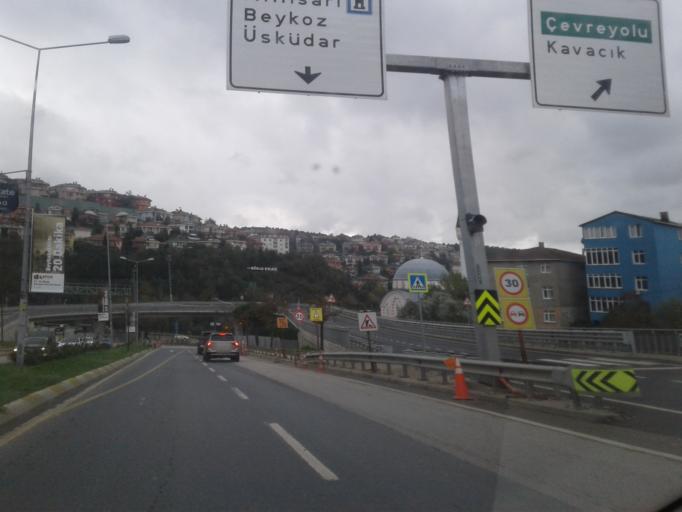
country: TR
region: Istanbul
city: Umraniye
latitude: 41.0866
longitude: 29.0852
